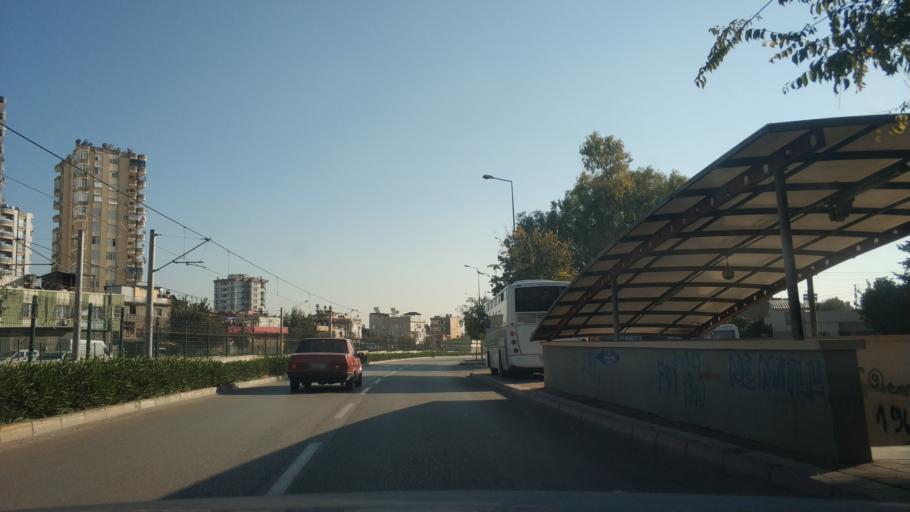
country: TR
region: Adana
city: Adana
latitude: 37.0224
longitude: 35.3017
